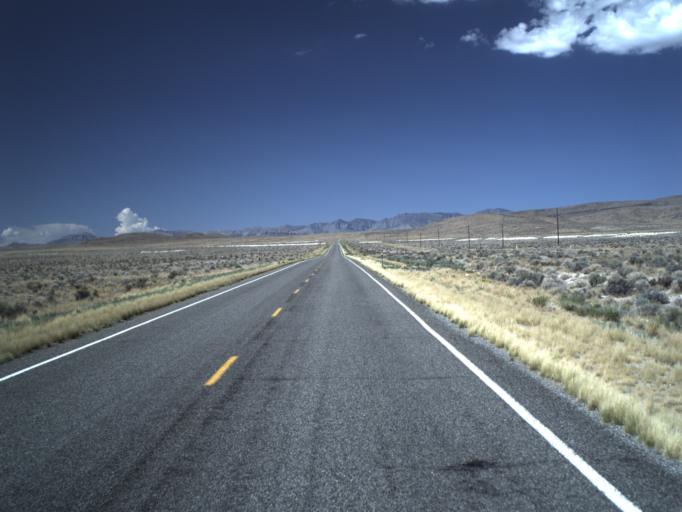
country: US
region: Utah
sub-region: Beaver County
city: Milford
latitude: 39.0671
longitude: -113.2298
